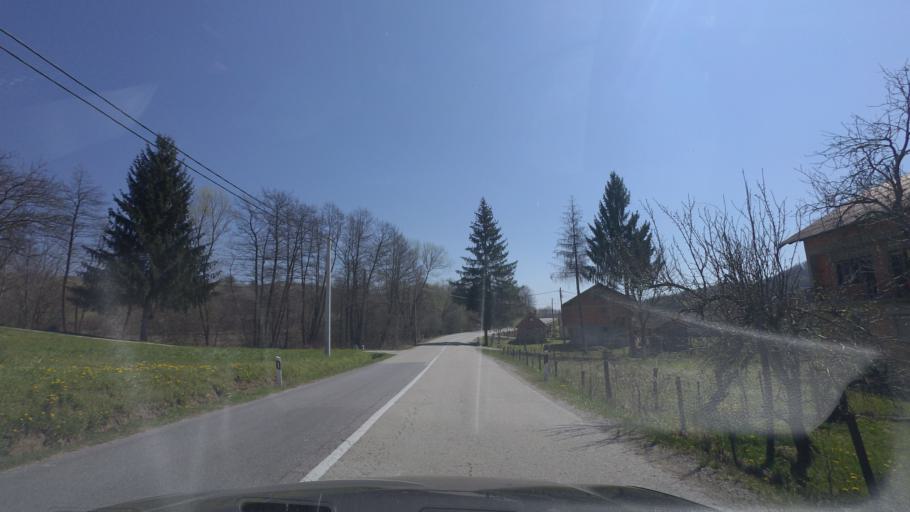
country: HR
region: Karlovacka
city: Vojnic
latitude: 45.3591
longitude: 15.6689
